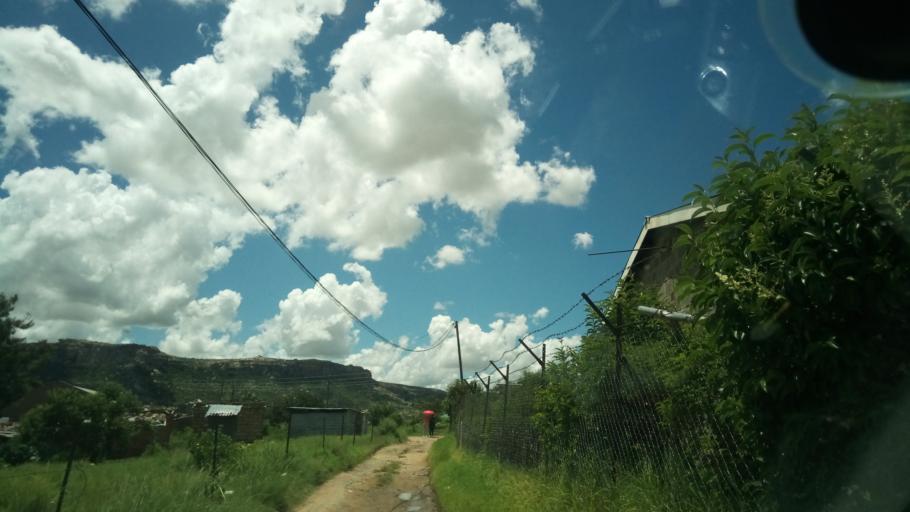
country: LS
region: Maseru
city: Maseru
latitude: -29.3510
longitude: 27.5340
